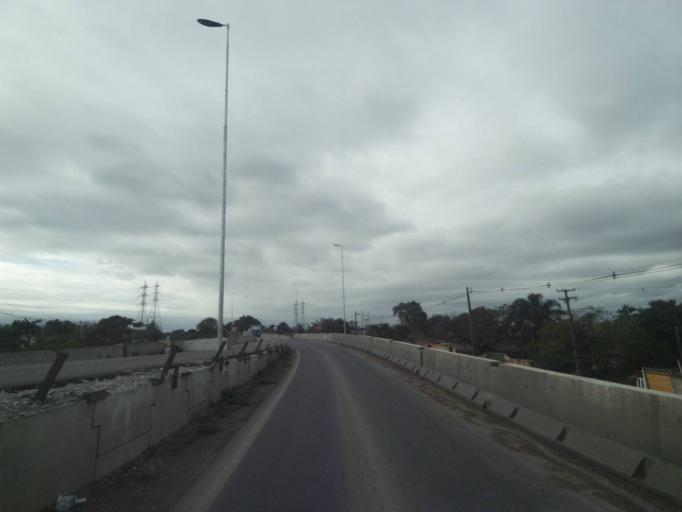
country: BR
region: Parana
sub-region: Paranagua
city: Paranagua
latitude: -25.5548
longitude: -48.5630
